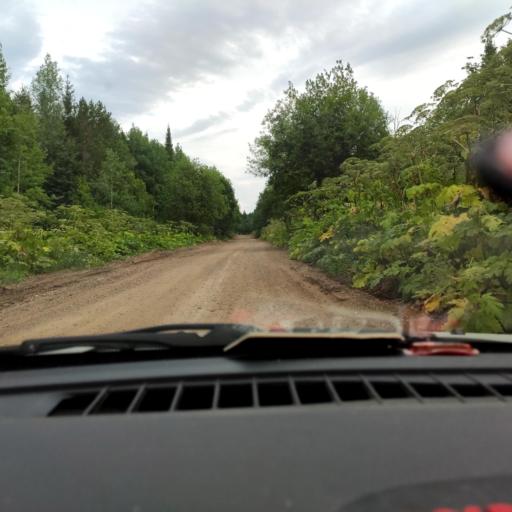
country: RU
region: Perm
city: Kultayevo
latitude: 57.8183
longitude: 56.0000
